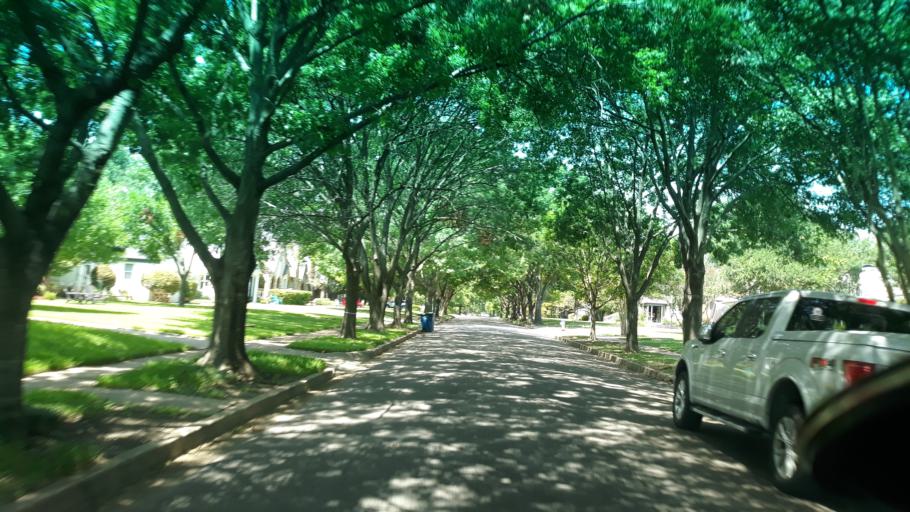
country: US
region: Texas
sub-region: Dallas County
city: Highland Park
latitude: 32.8129
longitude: -96.7389
